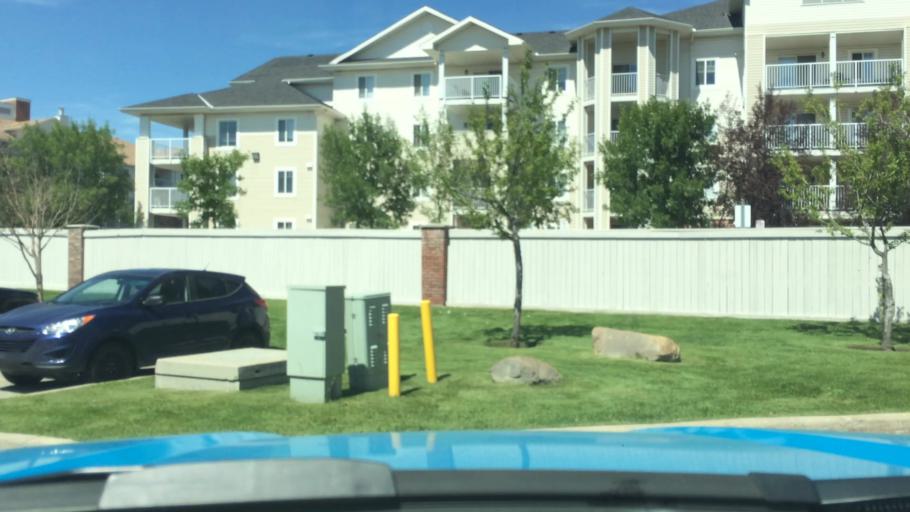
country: CA
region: Alberta
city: Calgary
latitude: 51.1555
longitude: -114.0535
